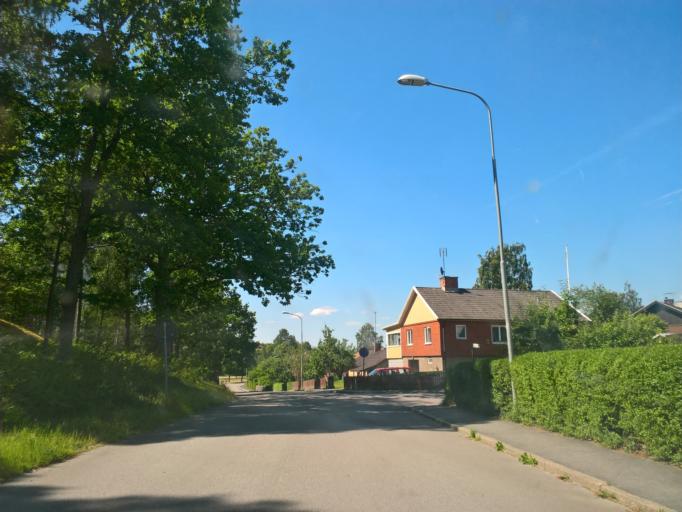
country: SE
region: OEstergoetland
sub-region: Finspangs Kommun
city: Finspang
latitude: 58.7086
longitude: 15.8034
